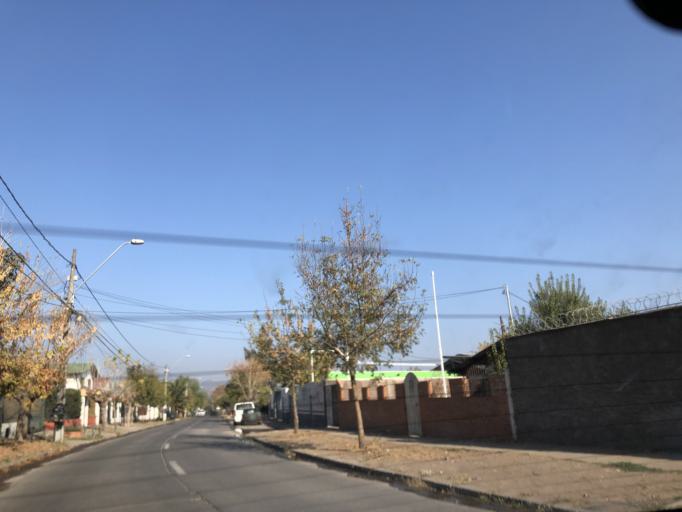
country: CL
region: Santiago Metropolitan
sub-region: Provincia de Cordillera
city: Puente Alto
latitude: -33.6268
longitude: -70.5822
